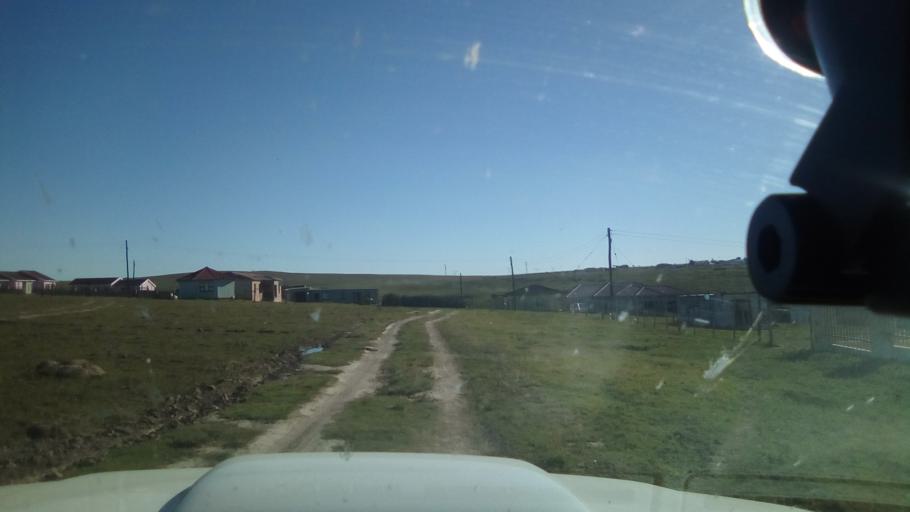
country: ZA
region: Eastern Cape
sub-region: Buffalo City Metropolitan Municipality
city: Bhisho
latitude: -32.9466
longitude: 27.2859
